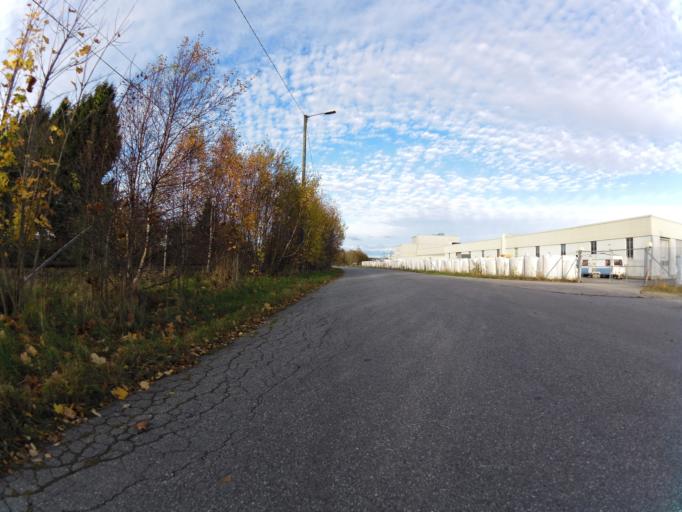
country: NO
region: Ostfold
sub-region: Fredrikstad
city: Fredrikstad
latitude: 59.2284
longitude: 10.9786
